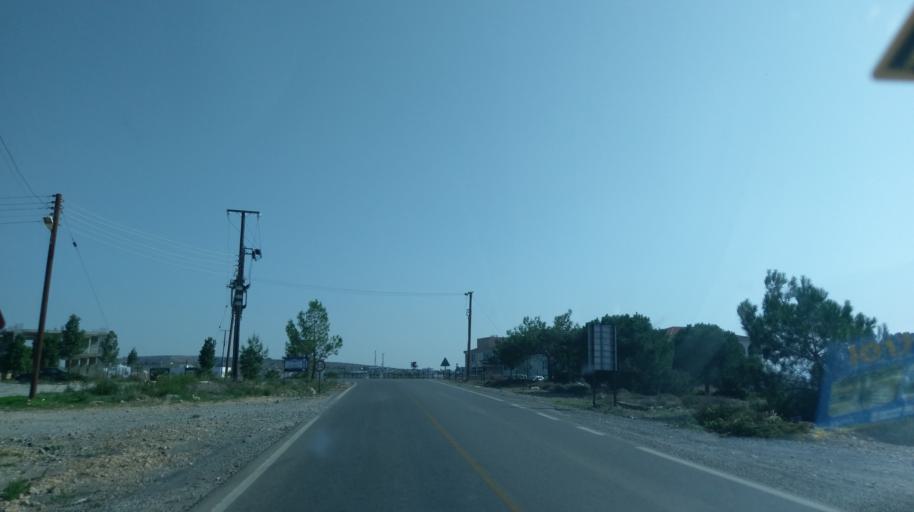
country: CY
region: Lefkosia
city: Morfou
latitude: 35.2513
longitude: 33.0328
